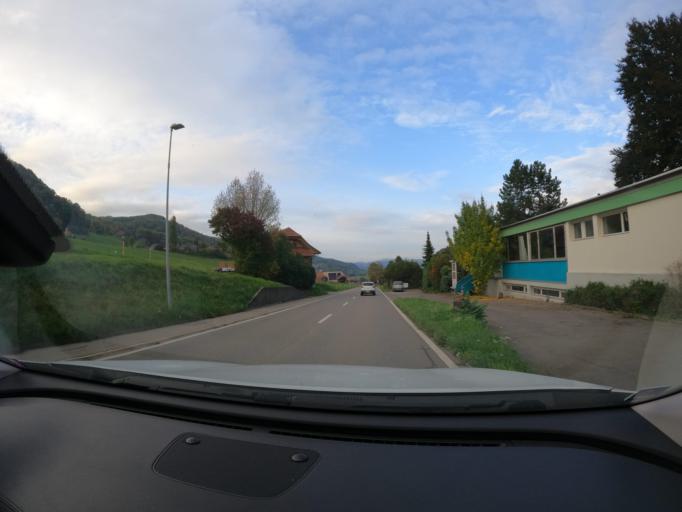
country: CH
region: Bern
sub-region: Bern-Mittelland District
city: Toffen
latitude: 46.8544
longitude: 7.4912
